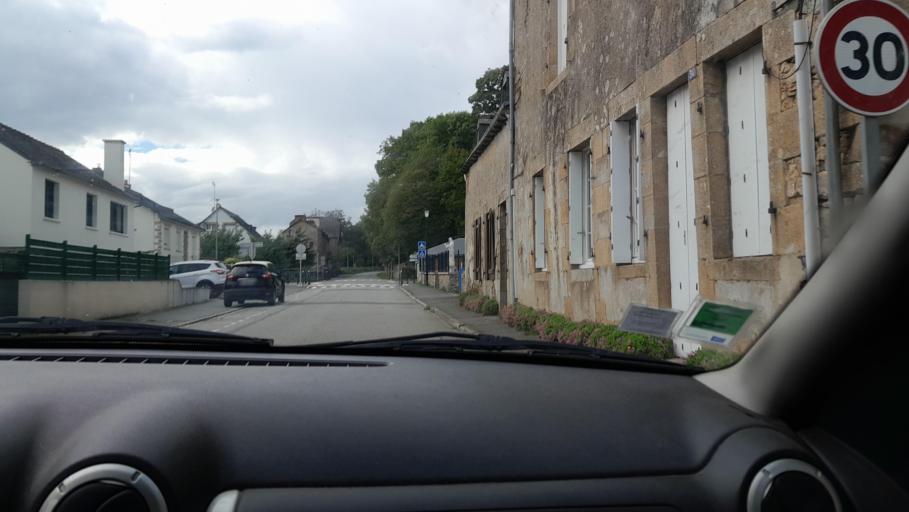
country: FR
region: Brittany
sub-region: Departement d'Ille-et-Vilaine
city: Le Pertre
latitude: 48.0355
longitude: -1.0387
